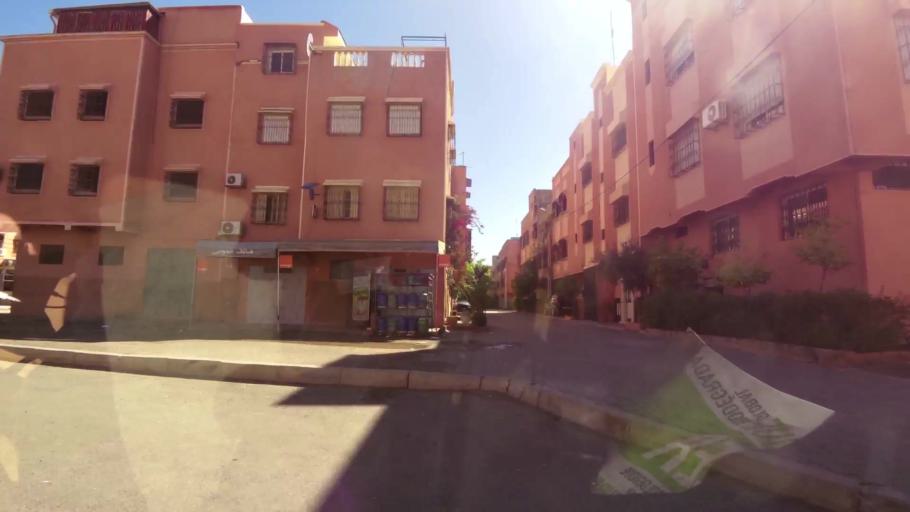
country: MA
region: Marrakech-Tensift-Al Haouz
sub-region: Marrakech
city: Marrakesh
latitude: 31.5936
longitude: -8.0464
